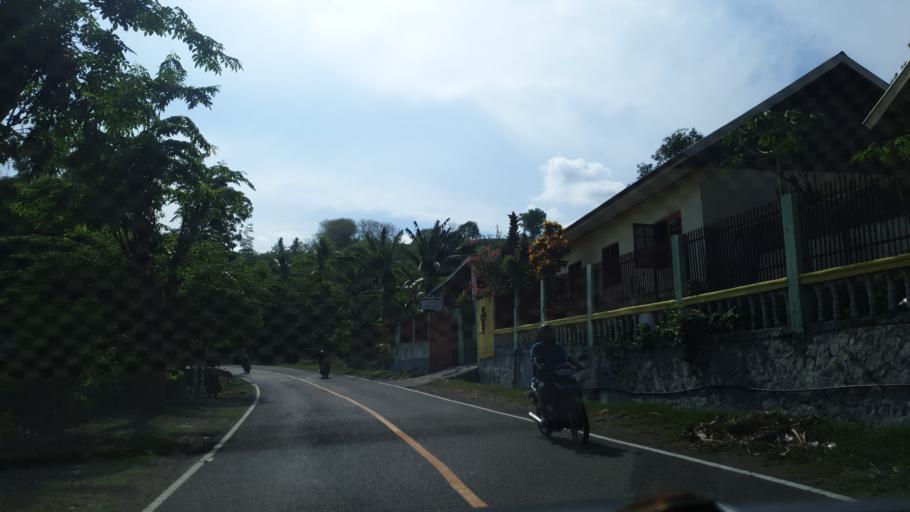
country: ID
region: East Nusa Tenggara
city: Nangalimang
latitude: -8.6579
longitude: 122.2008
